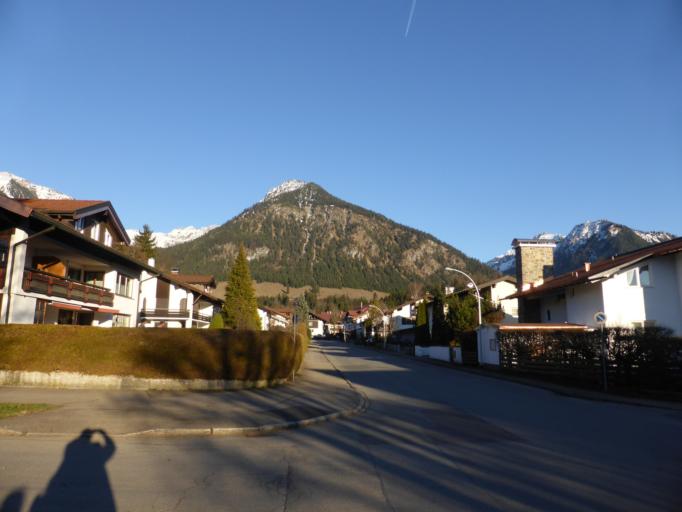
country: DE
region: Bavaria
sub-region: Swabia
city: Oberstdorf
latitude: 47.4039
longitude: 10.2758
